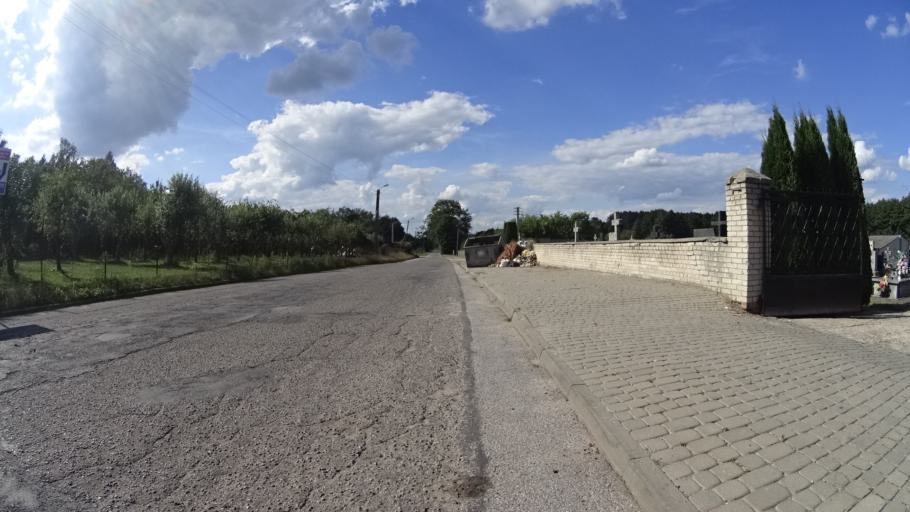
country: PL
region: Masovian Voivodeship
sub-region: Powiat grojecki
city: Mogielnica
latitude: 51.6995
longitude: 20.7143
